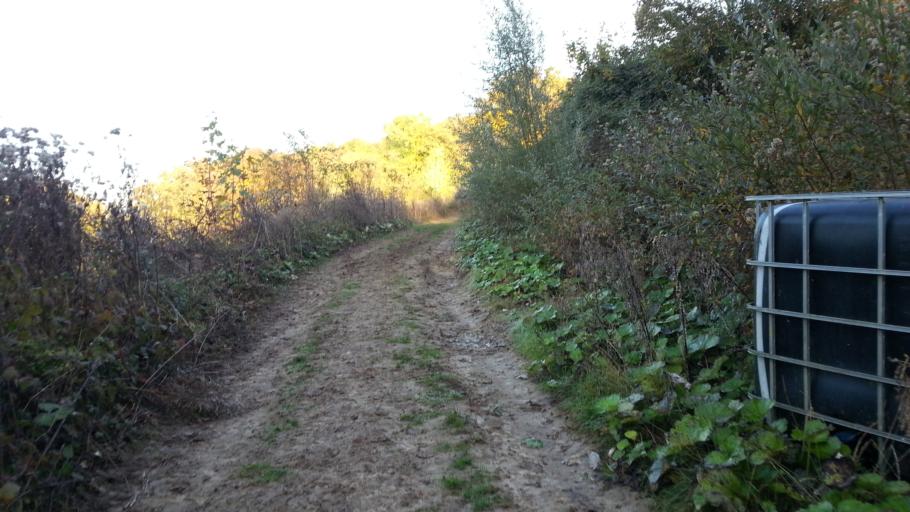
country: FR
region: Picardie
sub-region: Departement de l'Oise
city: Cires-les-Mello
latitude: 49.2844
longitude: 2.3480
